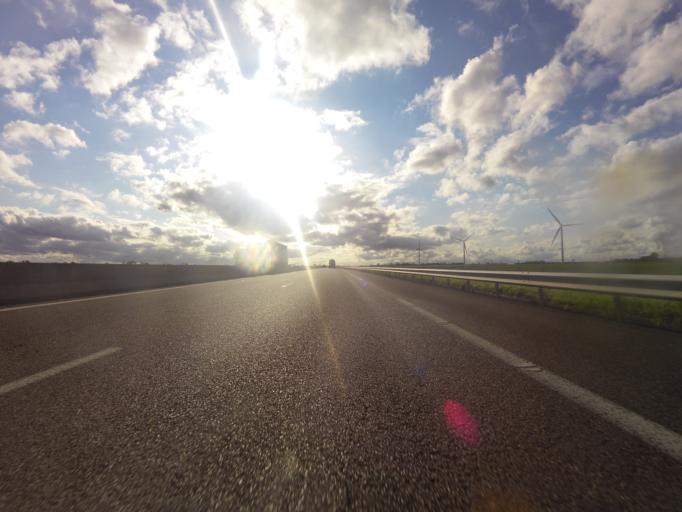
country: FR
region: Picardie
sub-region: Departement de la Somme
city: Beaucamps-le-Vieux
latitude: 49.8077
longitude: 1.8280
